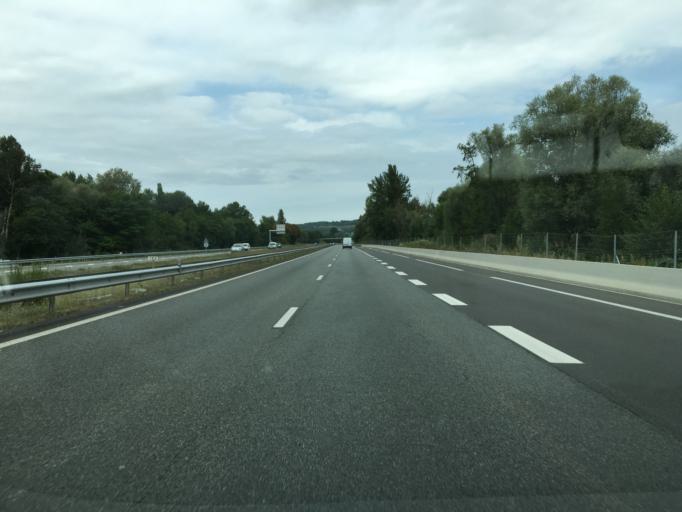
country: FR
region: Rhone-Alpes
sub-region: Departement de l'Isere
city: Saint-Jean-de-Moirans
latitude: 45.3249
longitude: 5.6006
